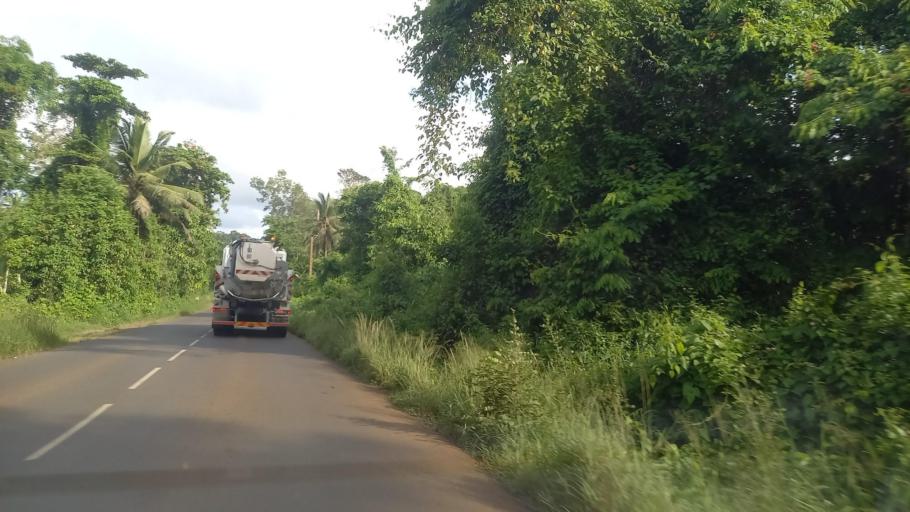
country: YT
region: Chiconi
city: Chiconi
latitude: -12.8142
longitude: 45.1276
